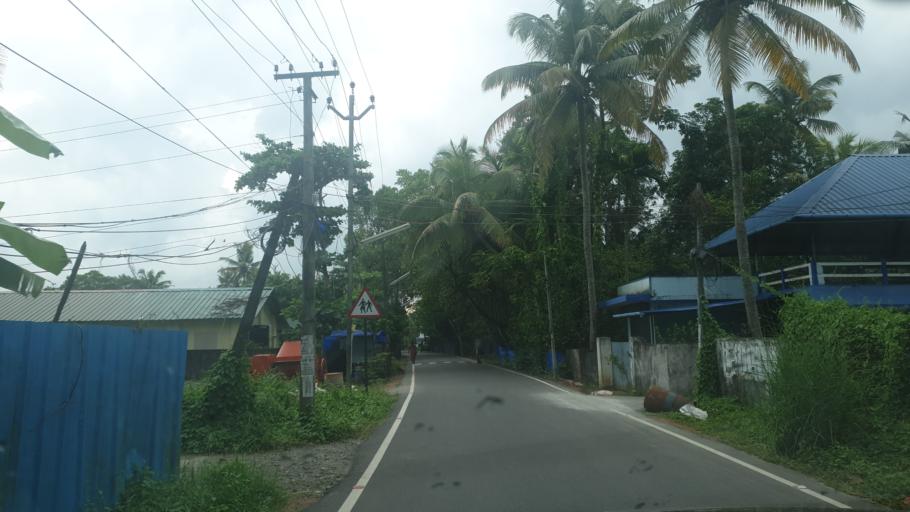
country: IN
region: Kerala
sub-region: Ernakulam
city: Cochin
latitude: 10.0027
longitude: 76.2269
